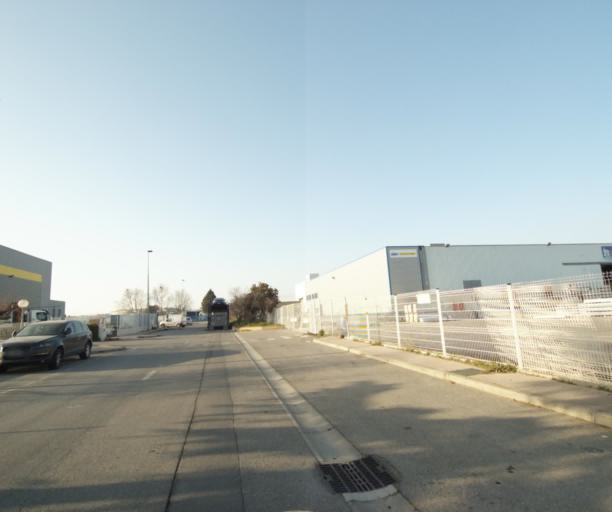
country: FR
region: Provence-Alpes-Cote d'Azur
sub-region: Departement des Bouches-du-Rhone
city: Saint-Victoret
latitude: 43.4291
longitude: 5.2450
